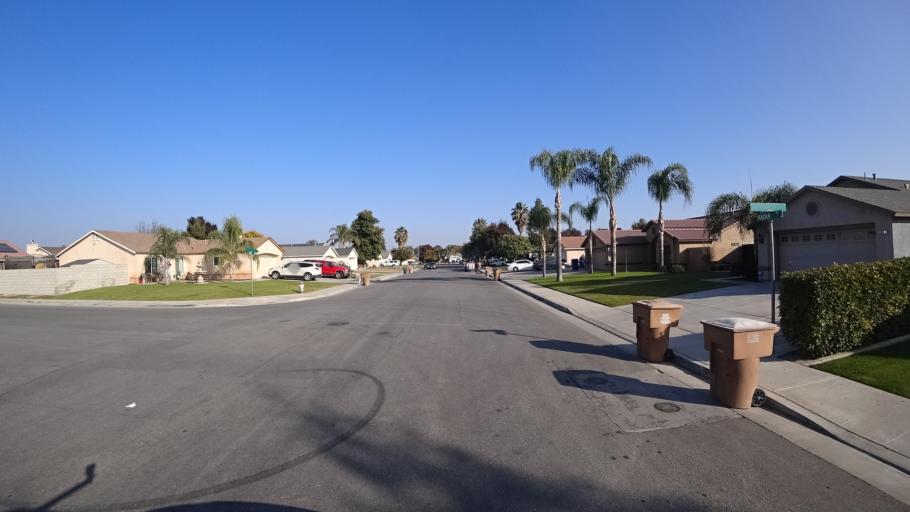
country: US
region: California
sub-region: Kern County
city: Greenfield
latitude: 35.2877
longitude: -119.0165
